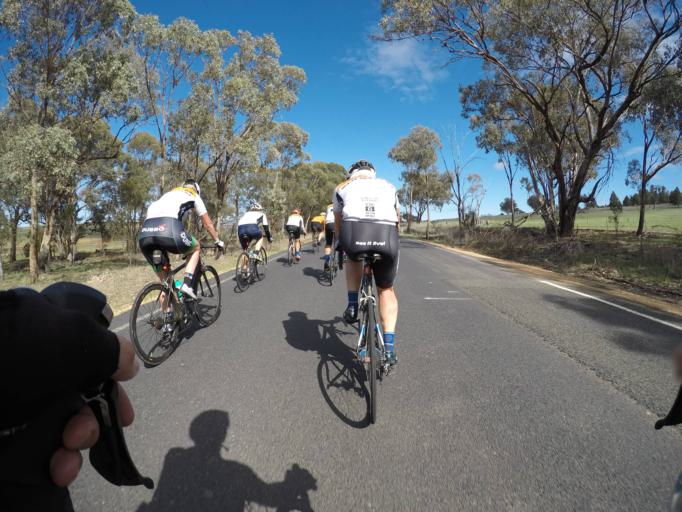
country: AU
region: New South Wales
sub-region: Parkes
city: Peak Hill
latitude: -32.7389
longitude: 148.5855
